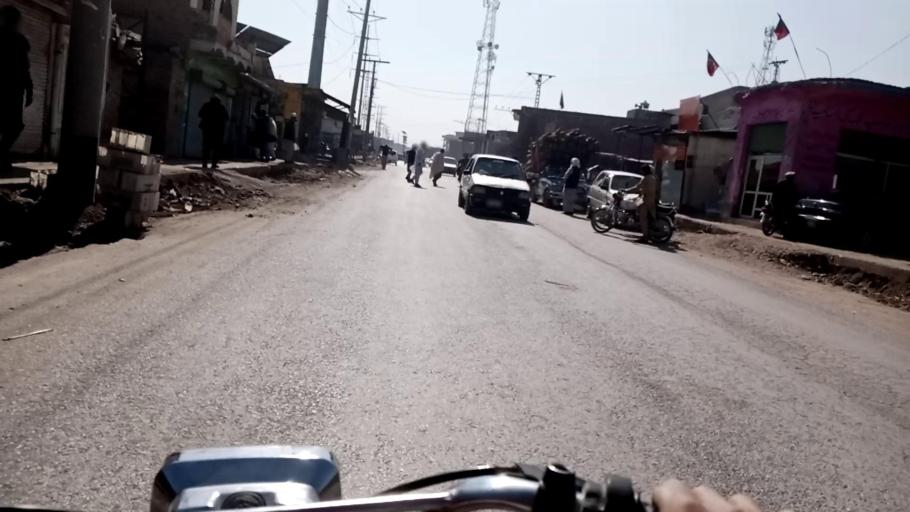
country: PK
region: Khyber Pakhtunkhwa
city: Peshawar
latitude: 33.9191
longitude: 71.4606
